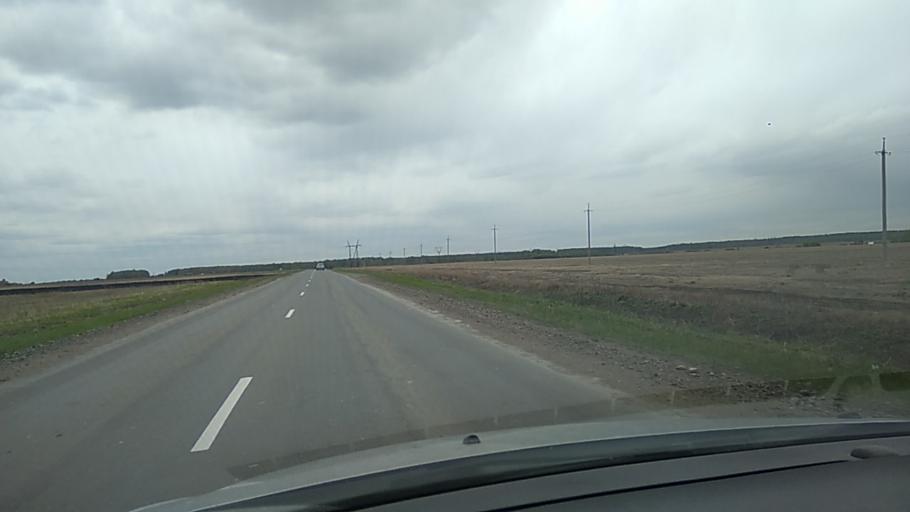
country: RU
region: Sverdlovsk
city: Martyush
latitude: 56.4101
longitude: 61.8046
